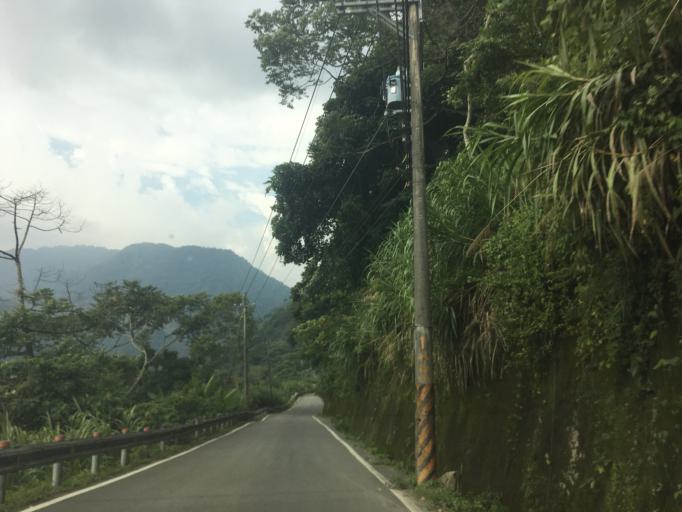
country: TW
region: Taiwan
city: Fengyuan
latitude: 24.3457
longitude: 120.9434
